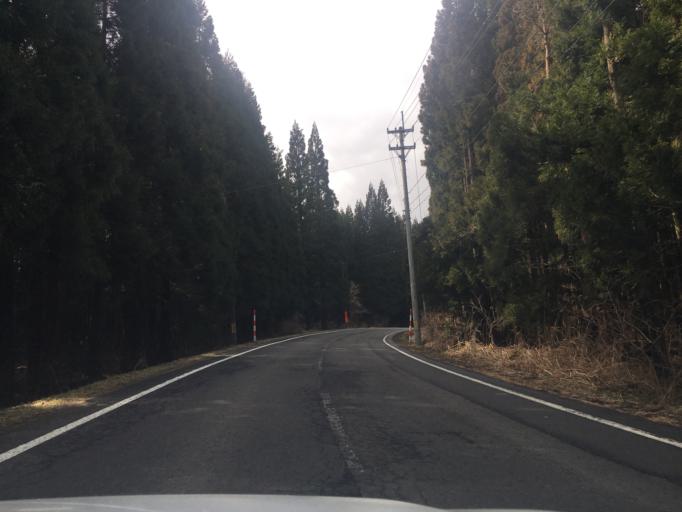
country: JP
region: Akita
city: Takanosu
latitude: 40.1798
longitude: 140.3573
